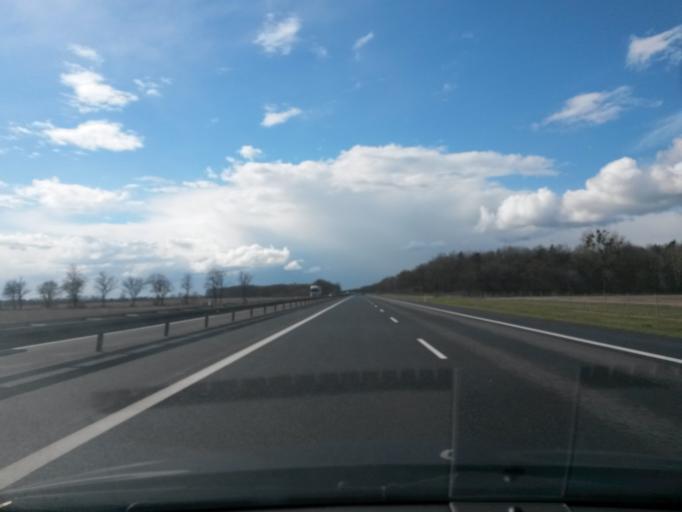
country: PL
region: Greater Poland Voivodeship
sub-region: Powiat wrzesinski
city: Wrzesnia
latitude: 52.3028
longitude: 17.6164
